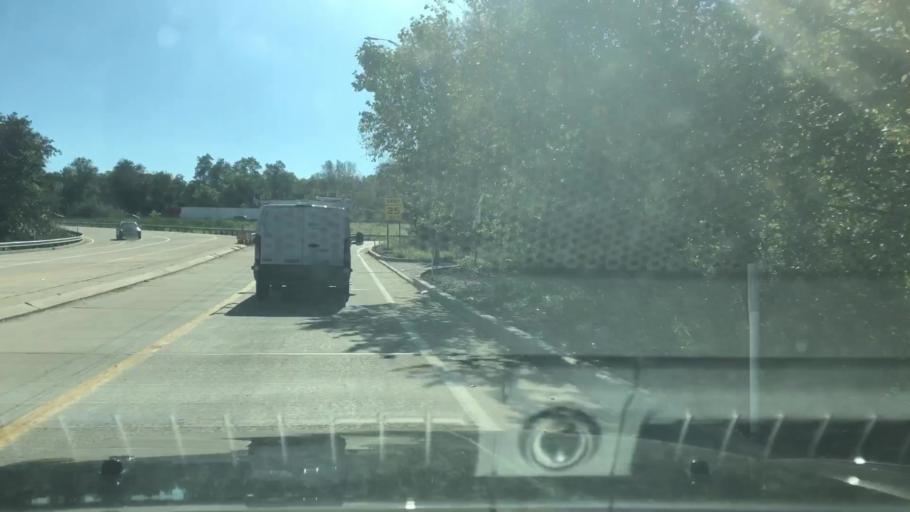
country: US
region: Pennsylvania
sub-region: Montgomery County
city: Dresher
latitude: 40.1399
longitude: -75.1715
